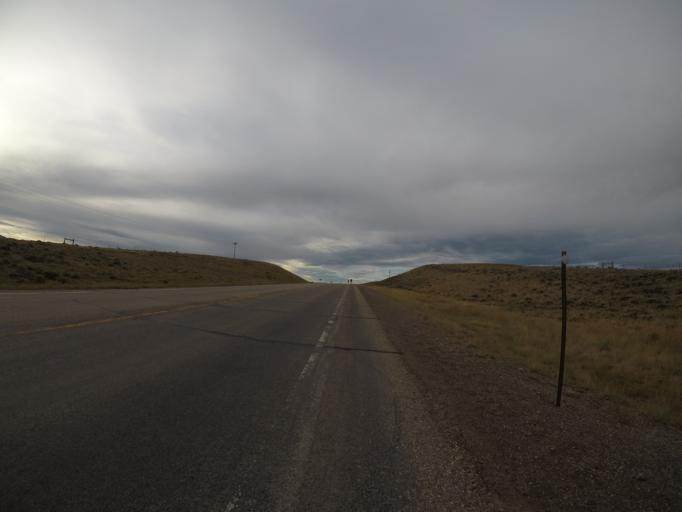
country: US
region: Wyoming
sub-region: Carbon County
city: Saratoga
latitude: 41.4242
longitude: -106.7953
